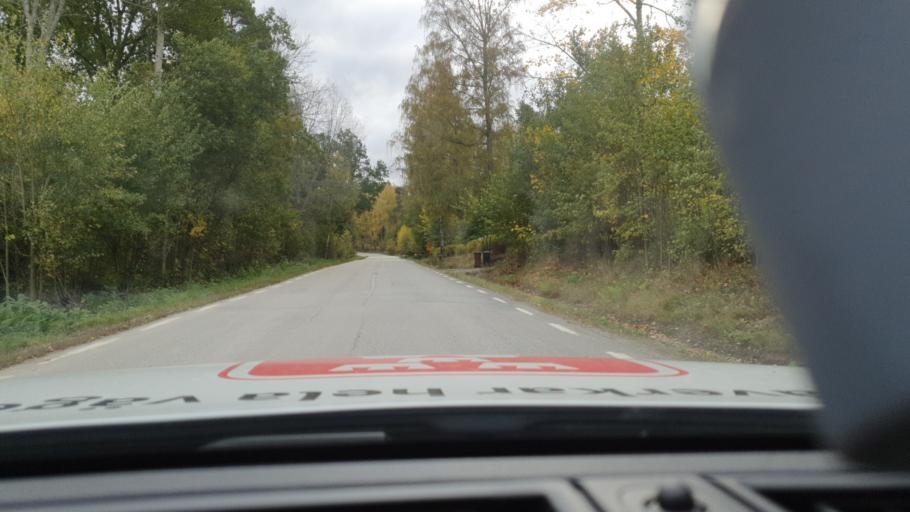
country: SE
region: Stockholm
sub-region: Upplands-Bro Kommun
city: Bro
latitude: 59.4987
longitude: 17.5677
